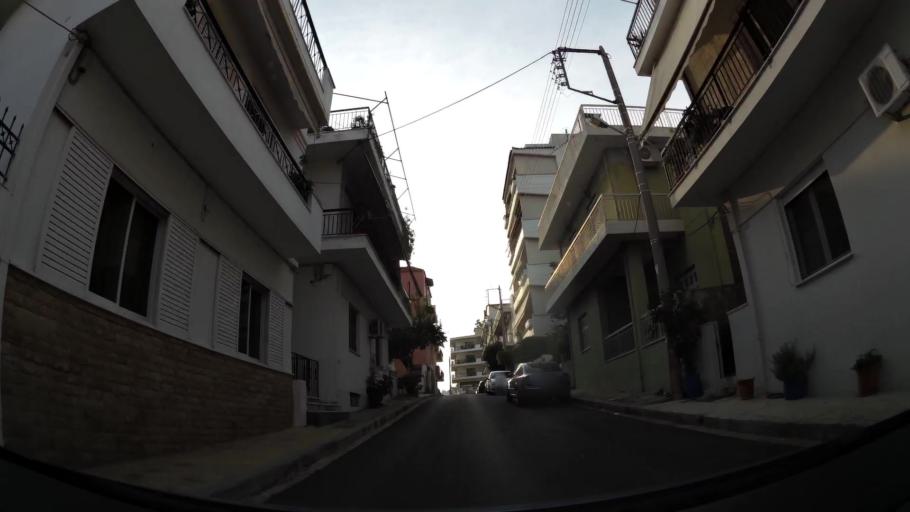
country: GR
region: Attica
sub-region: Nomarchia Athinas
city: Agios Dimitrios
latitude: 37.9388
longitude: 23.7259
